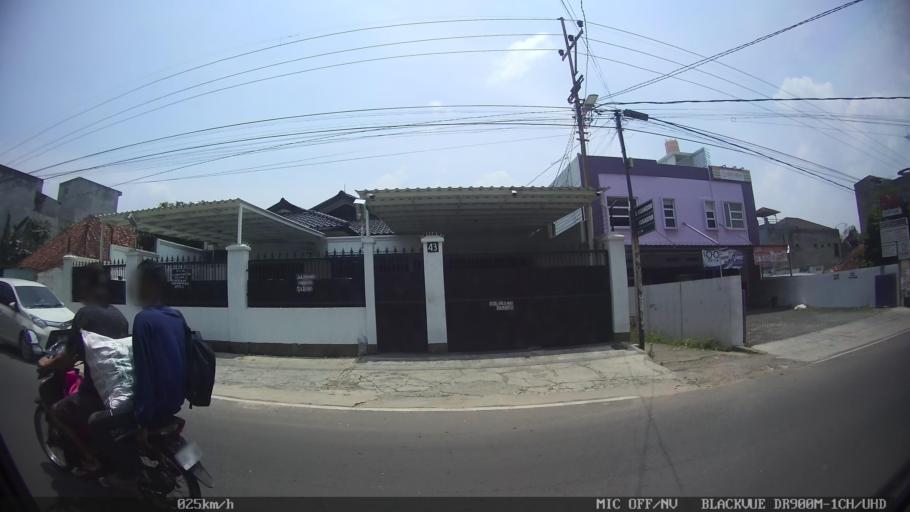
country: ID
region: Lampung
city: Bandarlampung
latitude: -5.4396
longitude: 105.2680
